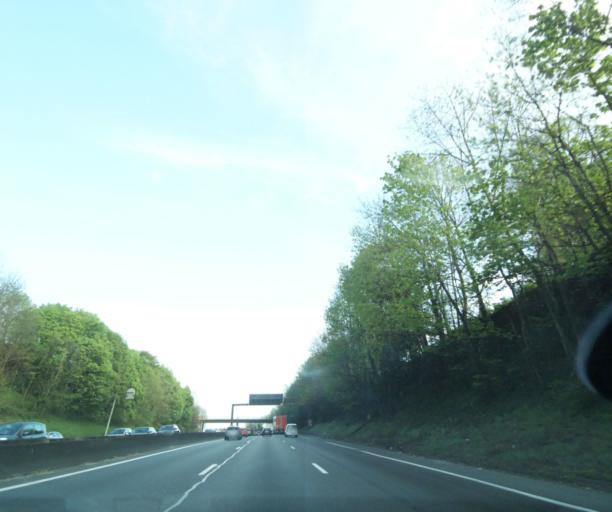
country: FR
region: Ile-de-France
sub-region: Departement de l'Essonne
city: Savigny-sur-Orge
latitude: 48.6738
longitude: 2.3427
